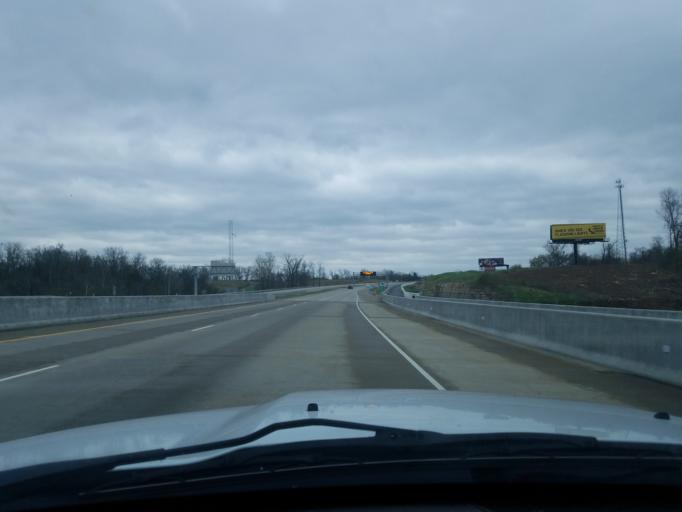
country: US
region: Kentucky
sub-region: Jefferson County
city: Prospect
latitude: 38.3499
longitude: -85.6603
